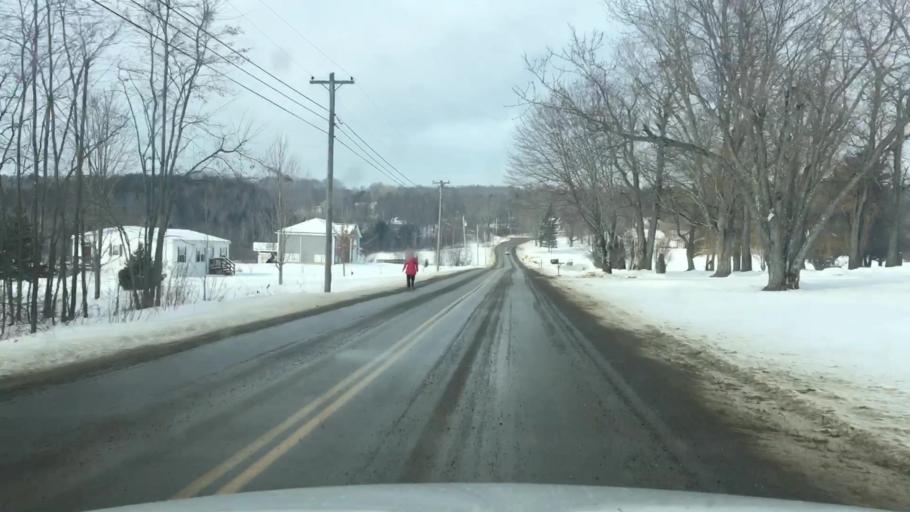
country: US
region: Maine
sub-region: Penobscot County
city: Hermon
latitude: 44.7661
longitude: -68.9563
